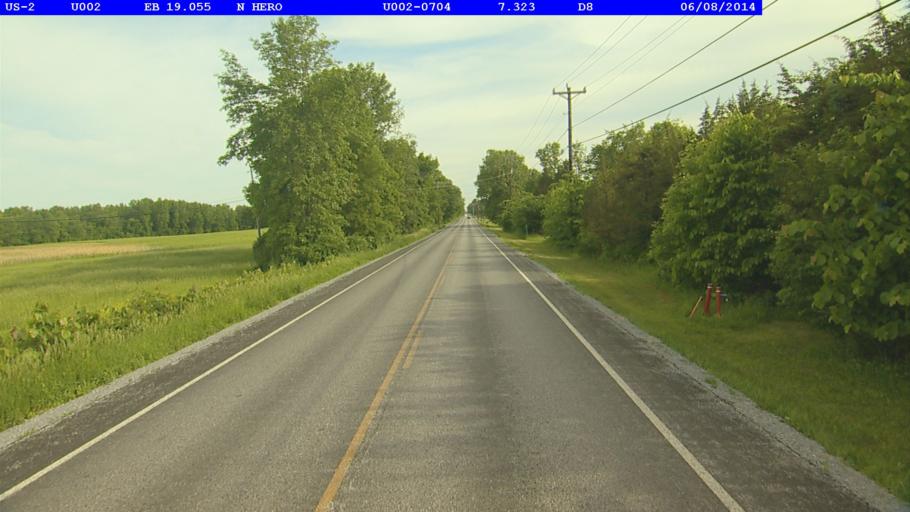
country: US
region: Vermont
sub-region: Grand Isle County
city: North Hero
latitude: 44.7941
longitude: -73.2925
